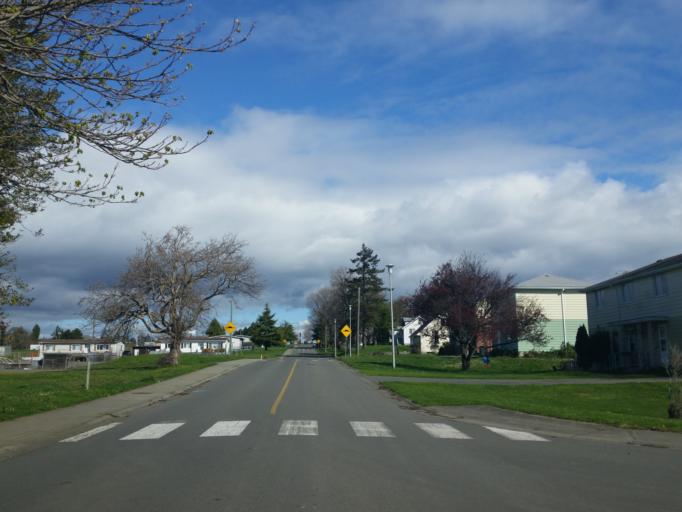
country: CA
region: British Columbia
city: Victoria
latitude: 48.4198
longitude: -123.4050
